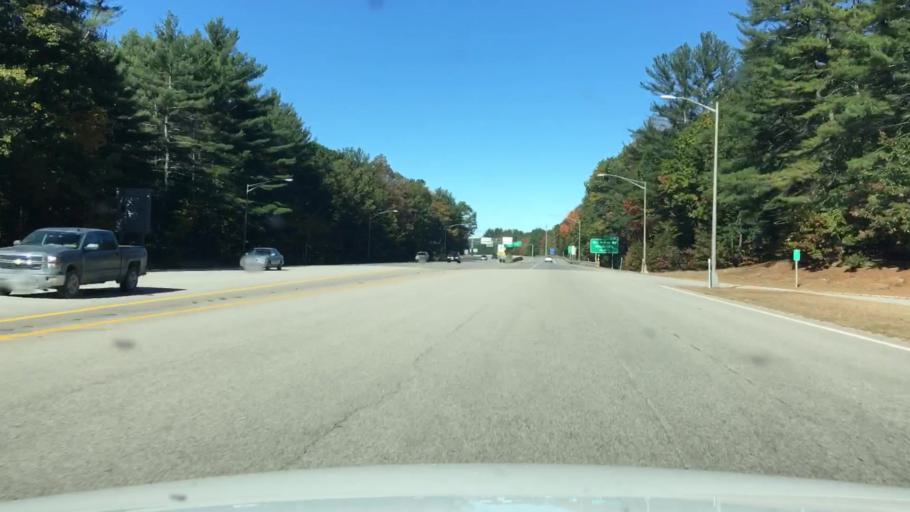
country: US
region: New Hampshire
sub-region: Strafford County
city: Rochester
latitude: 43.2747
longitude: -70.9643
